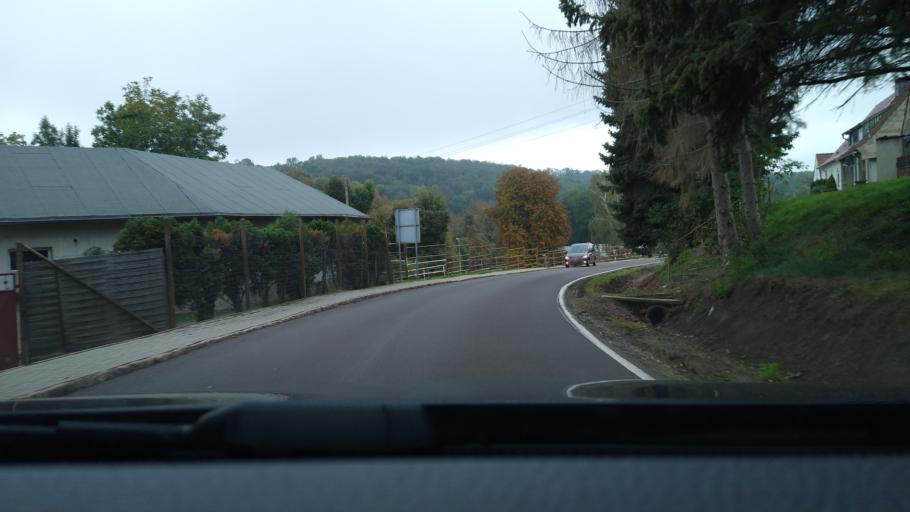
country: DE
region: Saxony-Anhalt
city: Polleben
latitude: 51.6046
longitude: 11.6158
